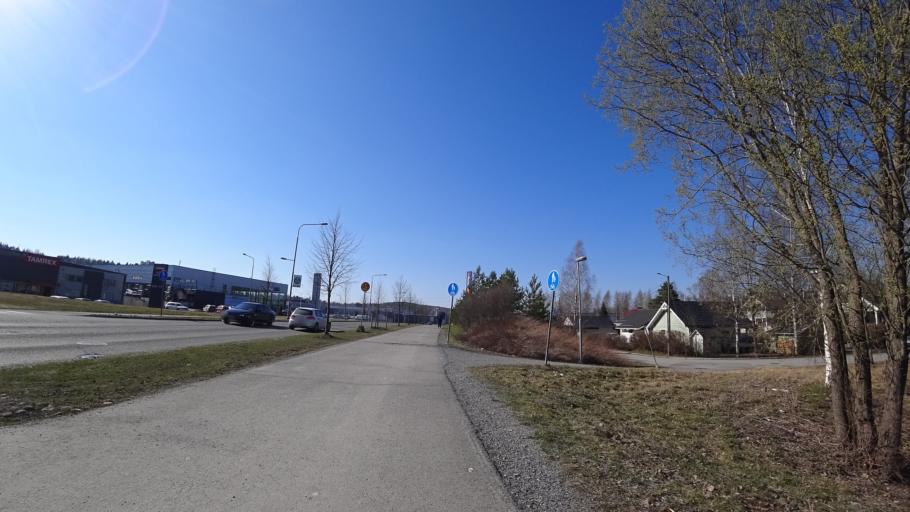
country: FI
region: Pirkanmaa
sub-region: Tampere
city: Pirkkala
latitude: 61.5188
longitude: 23.6610
